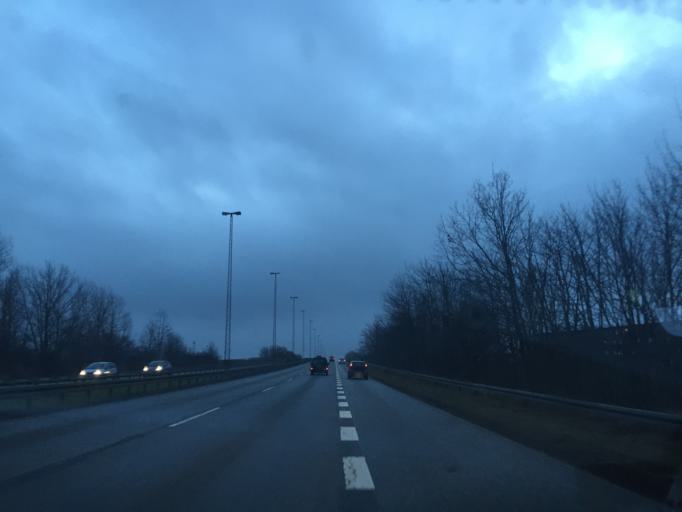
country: DK
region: Capital Region
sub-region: Hoje-Taastrup Kommune
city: Taastrup
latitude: 55.6530
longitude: 12.2823
